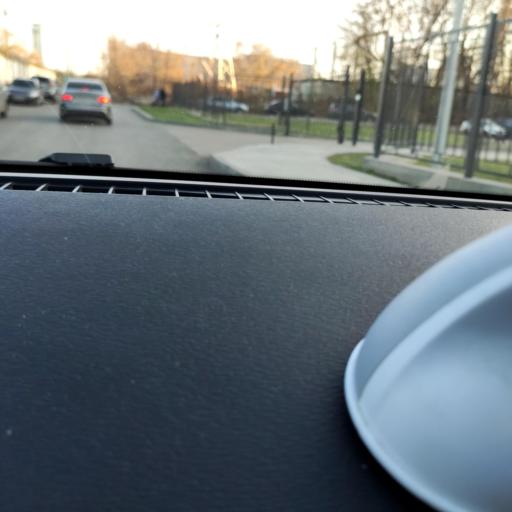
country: RU
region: Samara
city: Samara
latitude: 53.2100
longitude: 50.1446
